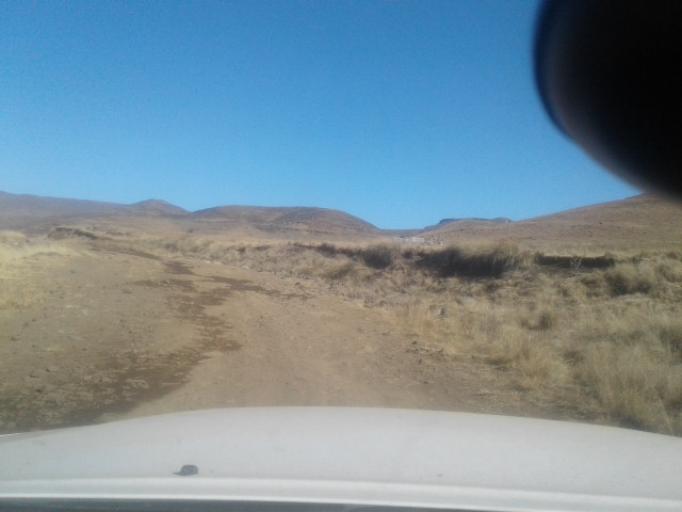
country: LS
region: Berea
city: Teyateyaneng
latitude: -29.3706
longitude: 28.0232
